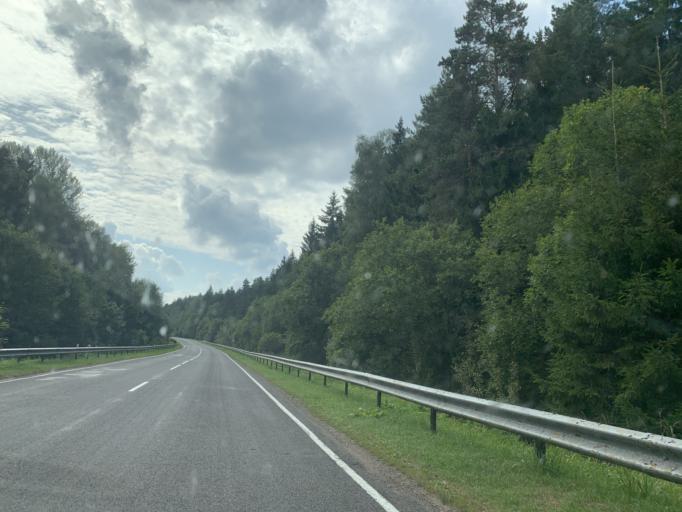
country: BY
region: Minsk
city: Novosel'ye
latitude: 53.8363
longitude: 27.1250
